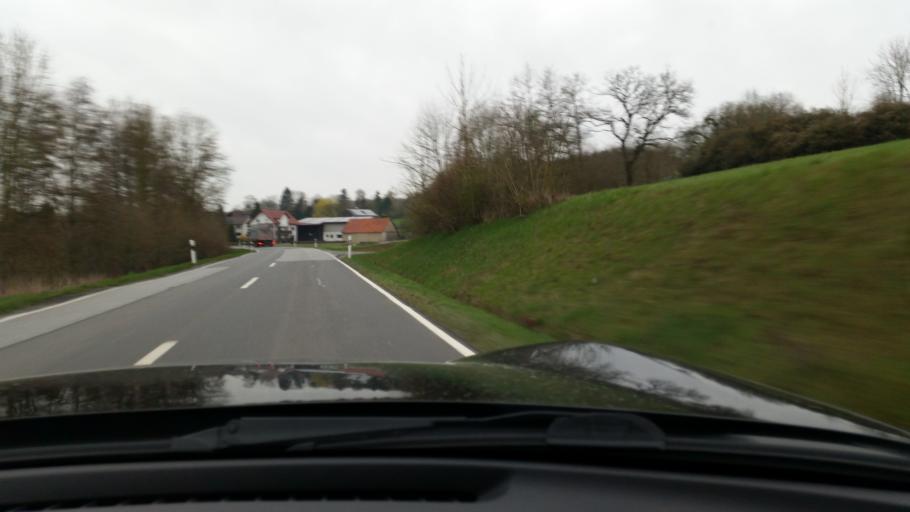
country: DE
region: Baden-Wuerttemberg
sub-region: Karlsruhe Region
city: Osterburken
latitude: 49.4685
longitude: 9.4151
